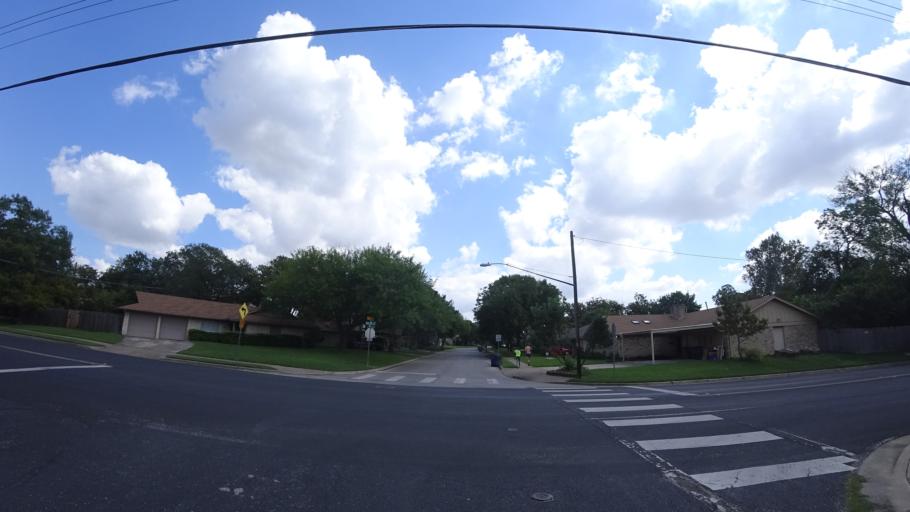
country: US
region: Texas
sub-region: Travis County
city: Austin
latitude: 30.3566
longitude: -97.7244
